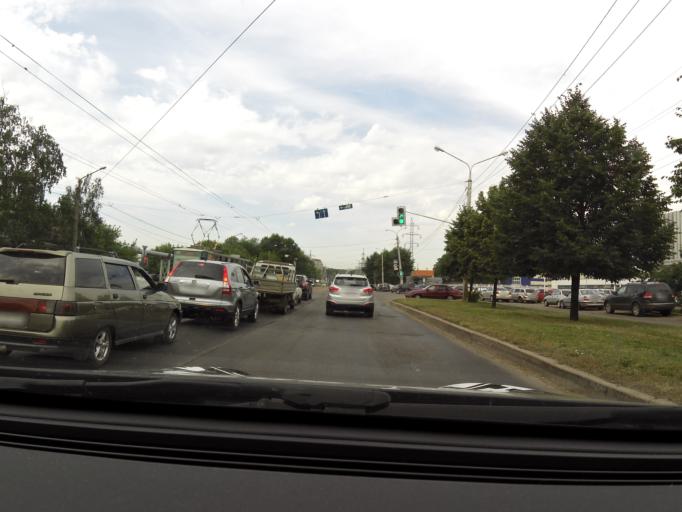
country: RU
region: Bashkortostan
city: Ufa
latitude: 54.7977
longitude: 56.0677
